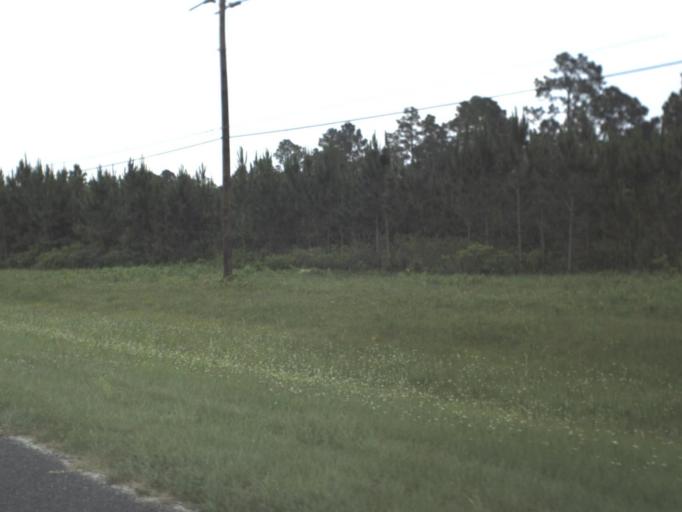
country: US
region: Florida
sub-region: Putnam County
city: Palatka
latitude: 29.6793
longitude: -81.6604
